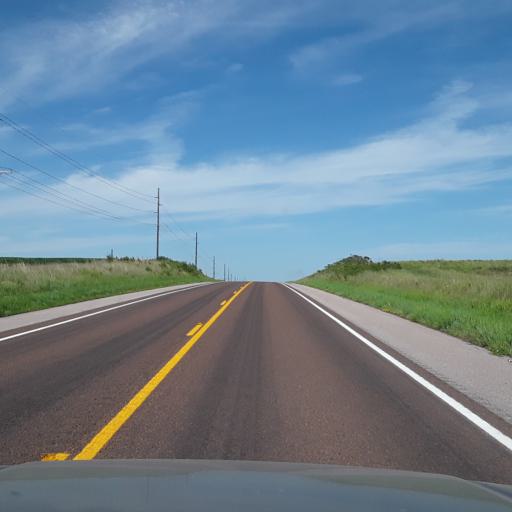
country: US
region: Nebraska
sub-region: Seward County
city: Milford
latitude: 40.8866
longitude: -96.8761
